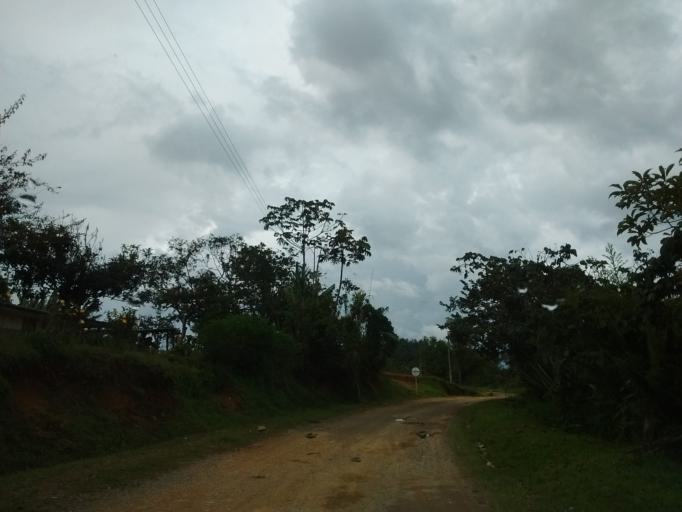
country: CO
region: Cauca
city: Cajibio
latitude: 2.5839
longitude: -76.6661
